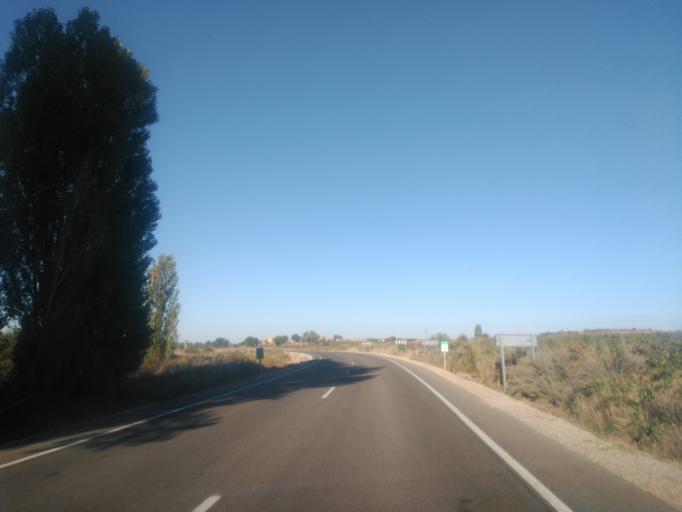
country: ES
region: Castille and Leon
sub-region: Provincia de Burgos
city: Zazuar
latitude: 41.6937
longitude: -3.5377
